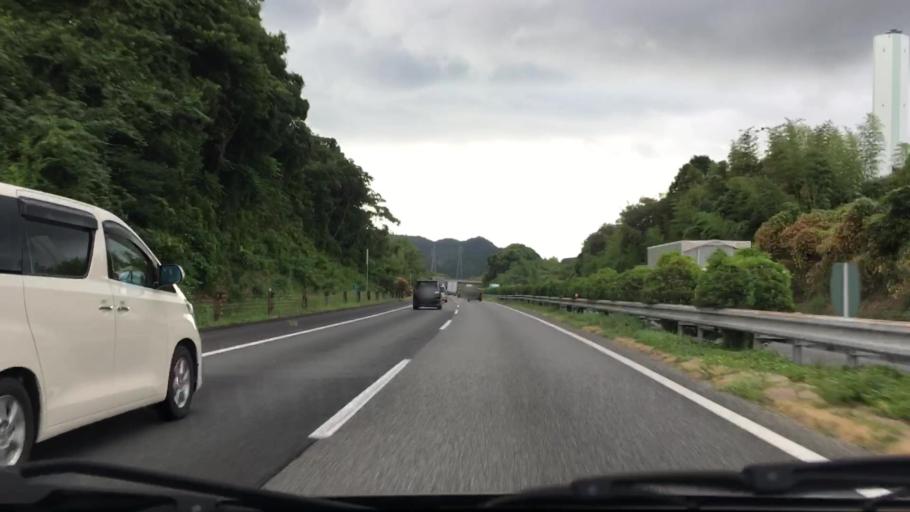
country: JP
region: Fukuoka
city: Sasaguri
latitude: 33.6403
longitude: 130.4881
